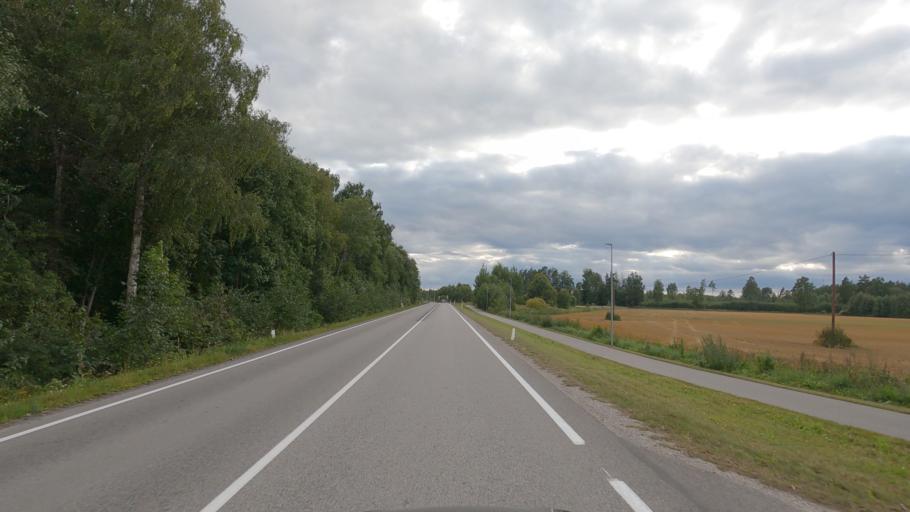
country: EE
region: Raplamaa
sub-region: Kohila vald
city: Kohila
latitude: 59.1782
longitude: 24.7721
